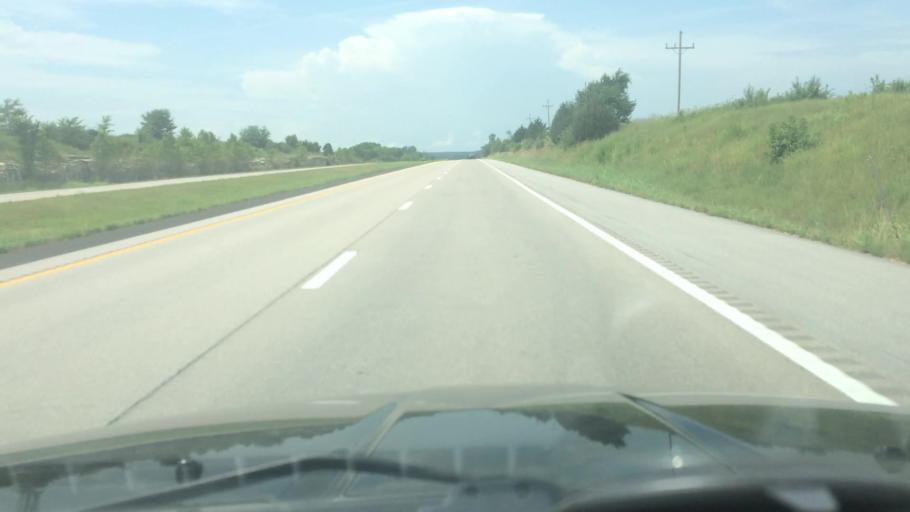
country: US
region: Missouri
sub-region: Polk County
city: Humansville
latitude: 37.8007
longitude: -93.5949
